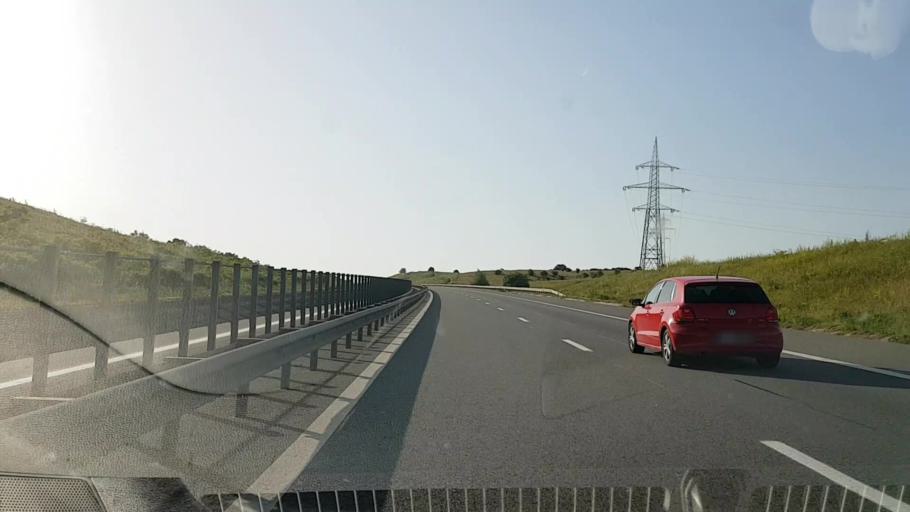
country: RO
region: Cluj
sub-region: Comuna Ciurila
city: Ciurila
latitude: 46.6497
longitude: 23.5123
